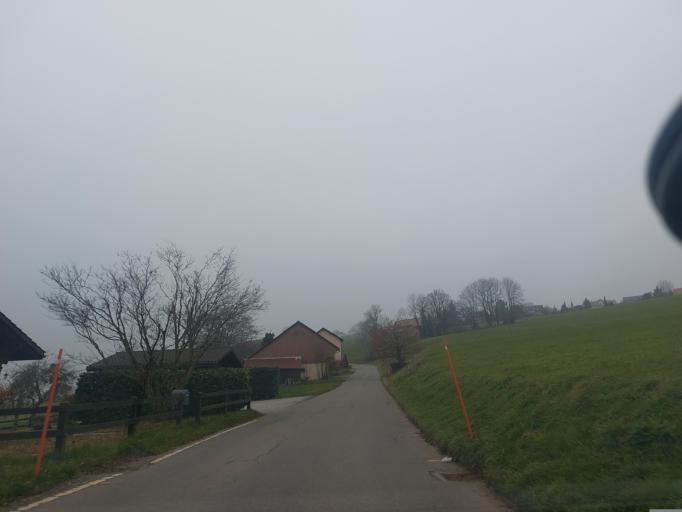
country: CH
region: Vaud
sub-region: Lavaux-Oron District
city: Oron-la-ville
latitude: 46.5756
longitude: 6.8769
